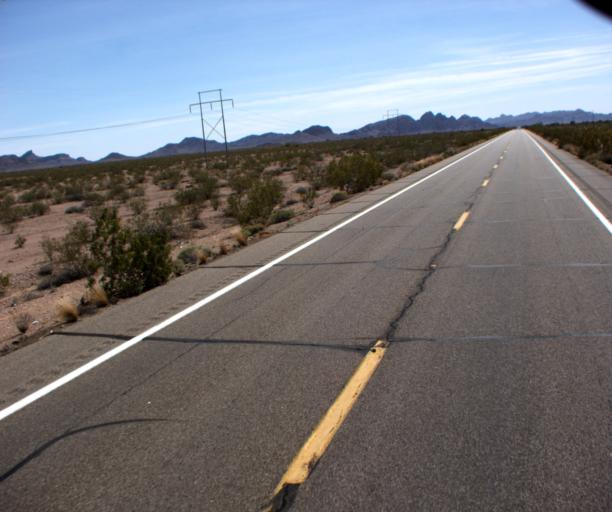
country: US
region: Arizona
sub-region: La Paz County
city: Quartzsite
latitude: 33.3623
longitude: -114.2171
